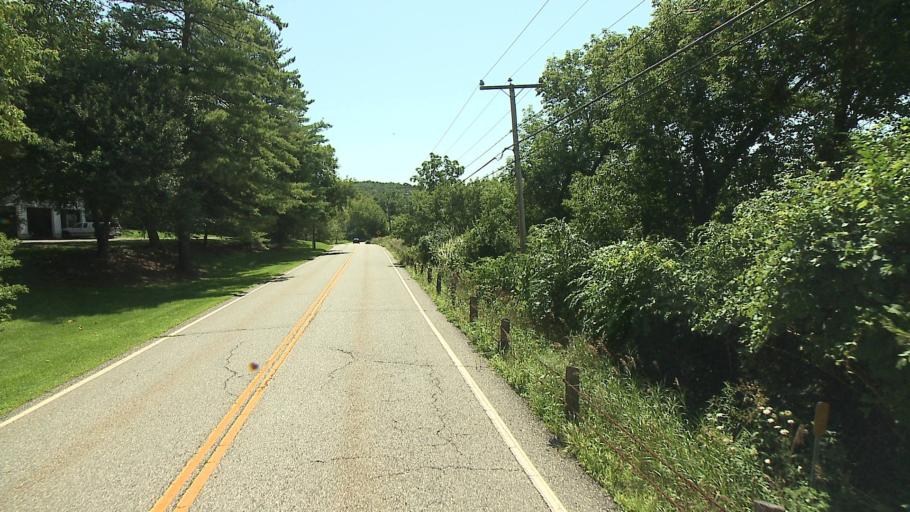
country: US
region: Connecticut
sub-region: Litchfield County
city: Kent
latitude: 41.8930
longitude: -73.4837
